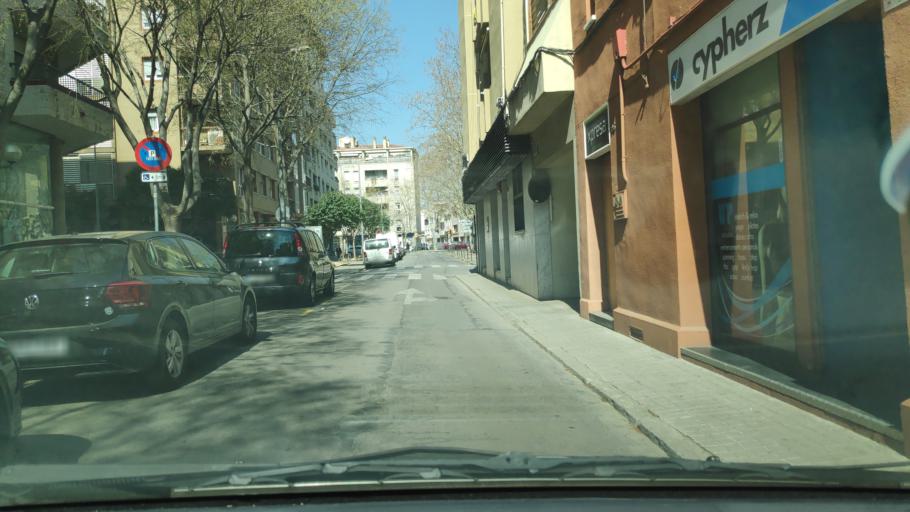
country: ES
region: Catalonia
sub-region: Provincia de Barcelona
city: Sabadell
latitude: 41.5505
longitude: 2.1041
